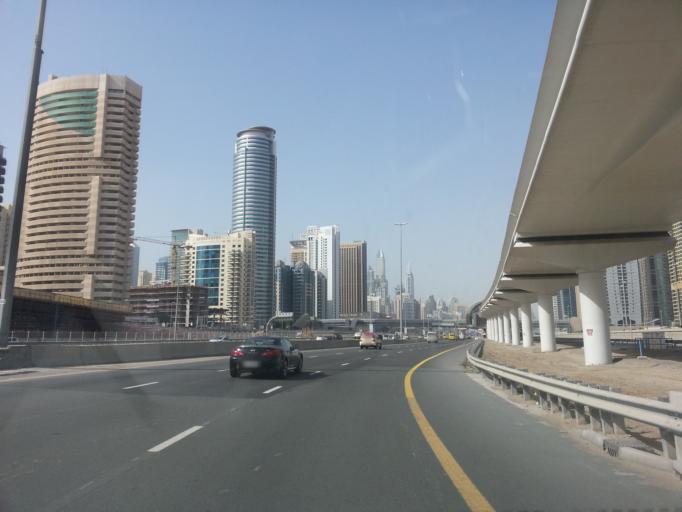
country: AE
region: Dubai
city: Dubai
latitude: 25.0676
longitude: 55.1358
